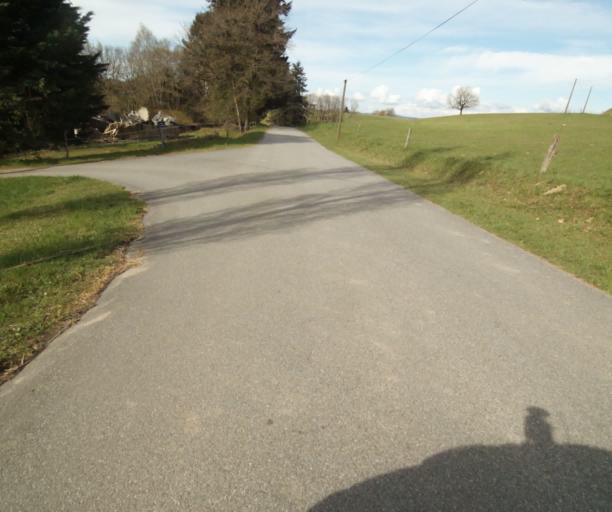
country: FR
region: Limousin
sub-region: Departement de la Correze
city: Correze
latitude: 45.3511
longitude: 1.8710
